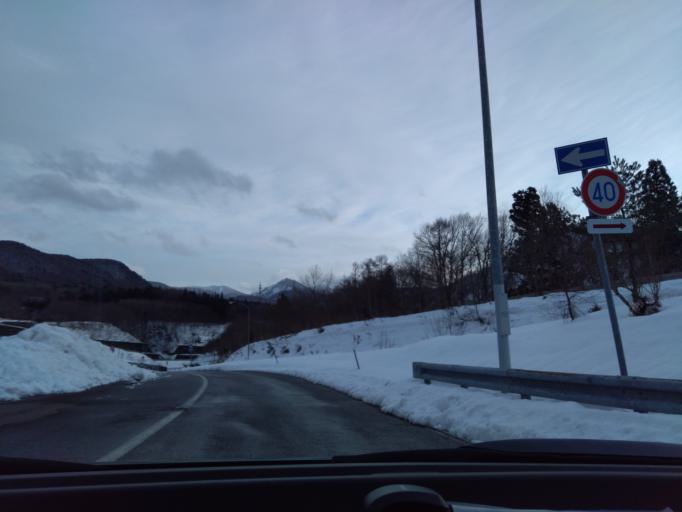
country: JP
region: Iwate
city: Kitakami
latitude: 39.2981
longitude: 140.8437
